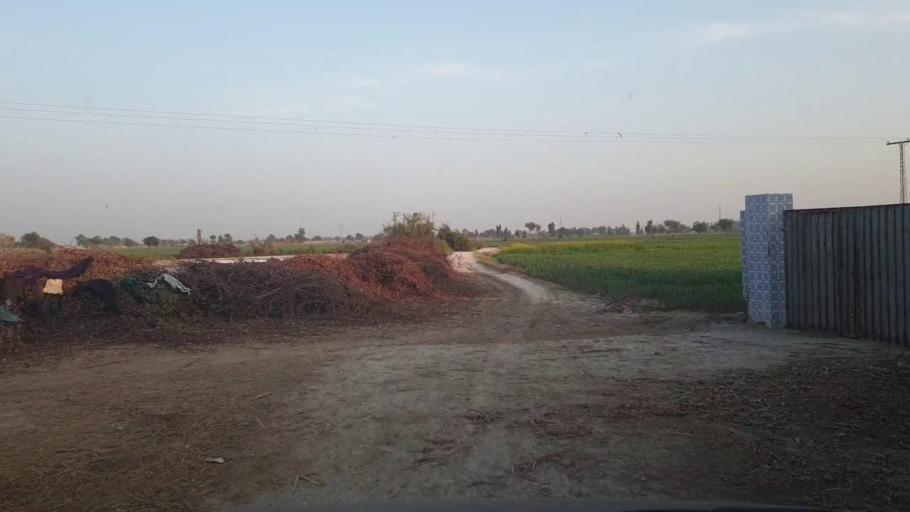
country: PK
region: Sindh
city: Bhit Shah
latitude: 25.8841
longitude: 68.5368
